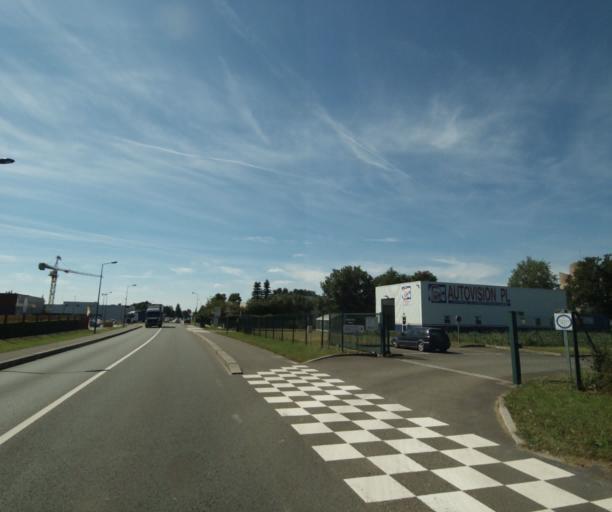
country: FR
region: Pays de la Loire
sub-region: Departement de la Mayenne
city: Saint-Berthevin
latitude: 48.0576
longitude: -0.8045
